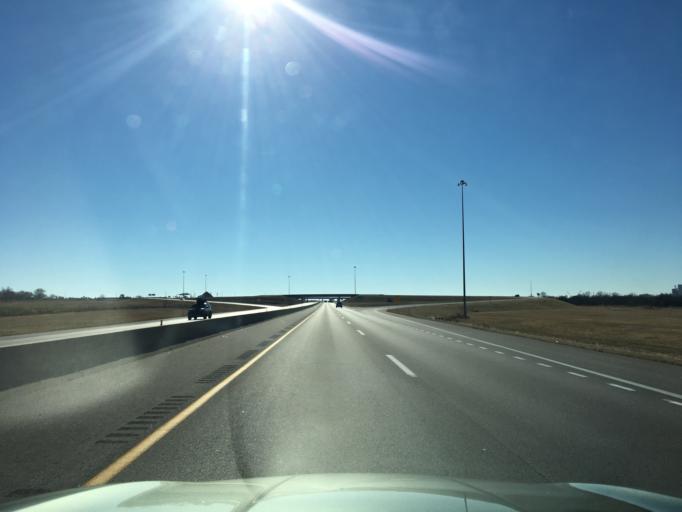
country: US
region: Kansas
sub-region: Sumner County
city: Wellington
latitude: 37.2835
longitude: -97.3403
